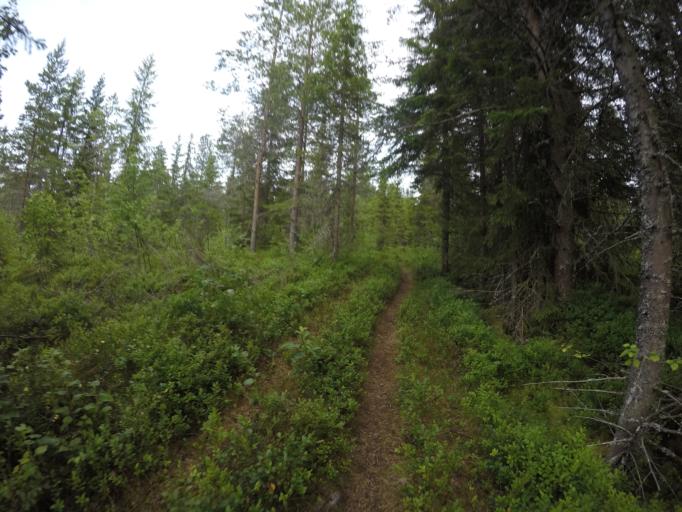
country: SE
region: Vaermland
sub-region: Filipstads Kommun
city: Lesjofors
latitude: 60.2047
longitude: 14.2762
